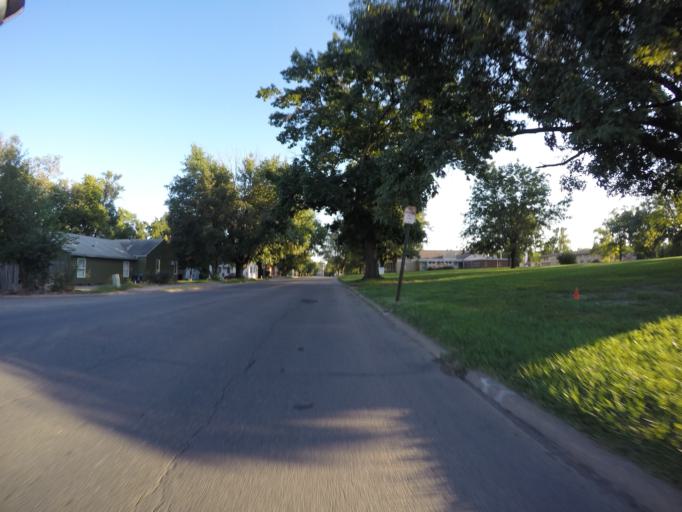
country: US
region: Kansas
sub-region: Riley County
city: Manhattan
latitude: 39.1914
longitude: -96.5890
